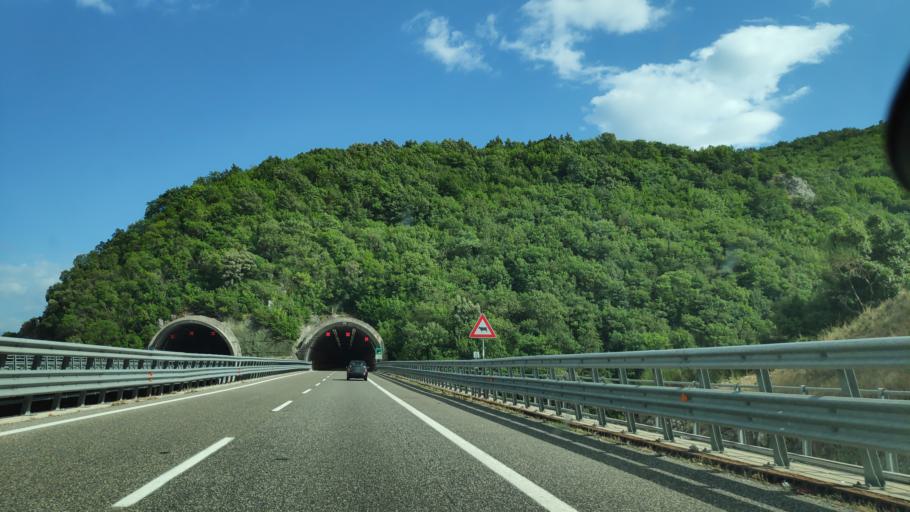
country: IT
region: Campania
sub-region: Provincia di Salerno
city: Sicignano degli Alburni
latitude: 40.6057
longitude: 15.2998
